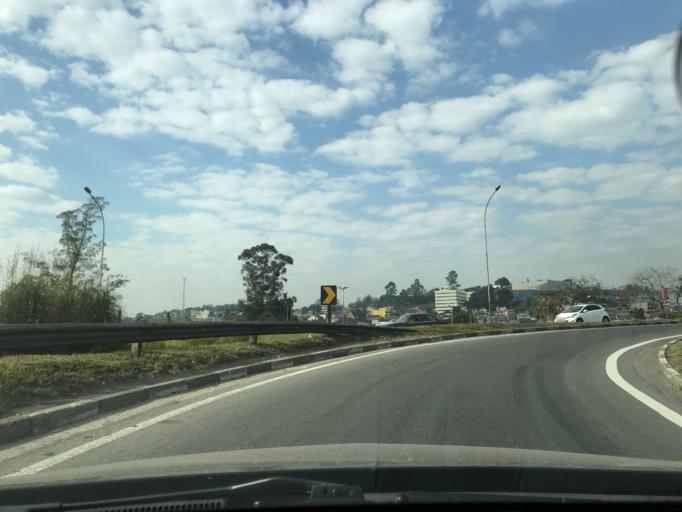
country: BR
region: Sao Paulo
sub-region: Cotia
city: Cotia
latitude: -23.6017
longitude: -46.9239
